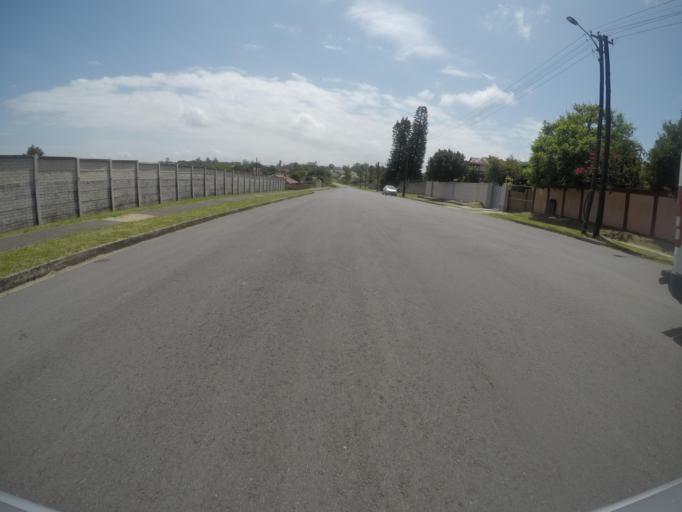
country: ZA
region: Eastern Cape
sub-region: Buffalo City Metropolitan Municipality
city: East London
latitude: -32.9723
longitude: 27.8654
